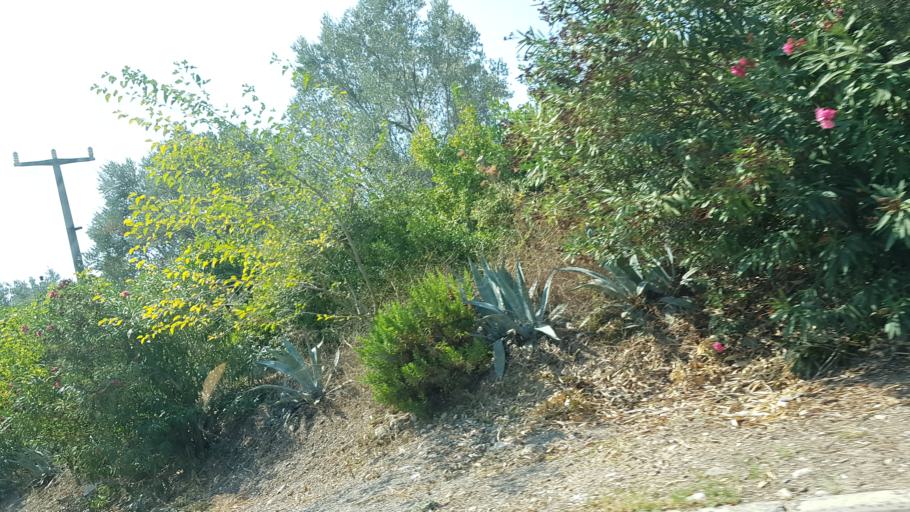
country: TR
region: Izmir
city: Urla
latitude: 38.3803
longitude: 26.7503
